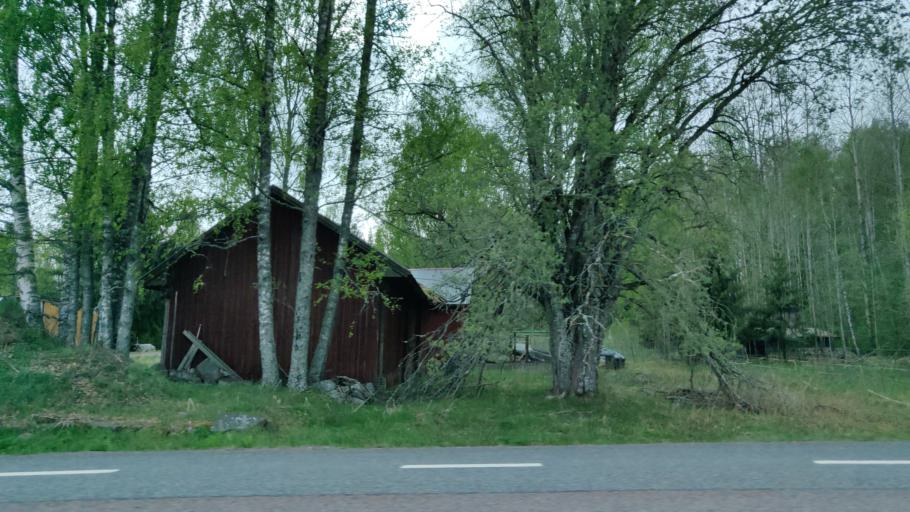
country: SE
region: Vaermland
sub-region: Forshaga Kommun
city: Deje
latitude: 59.6791
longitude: 13.4365
